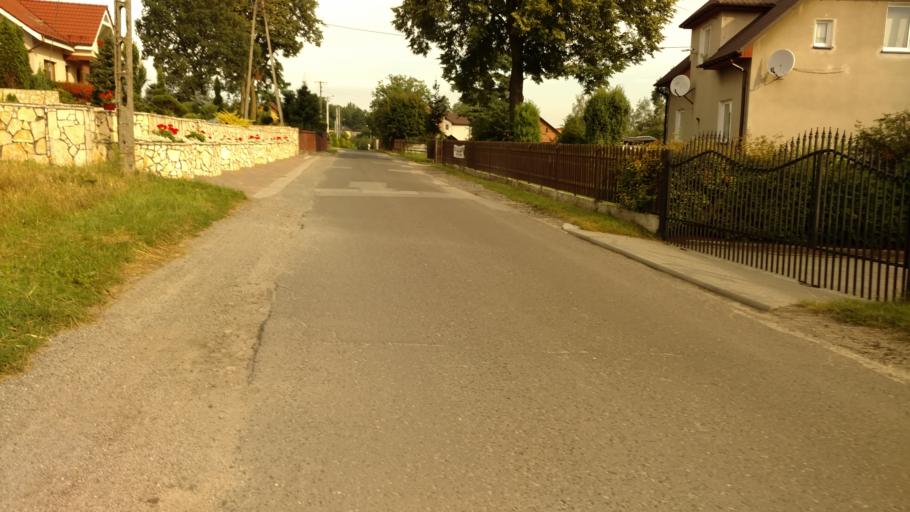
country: PL
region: Silesian Voivodeship
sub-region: Powiat pszczynski
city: Jankowice
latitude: 49.9981
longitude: 19.0027
